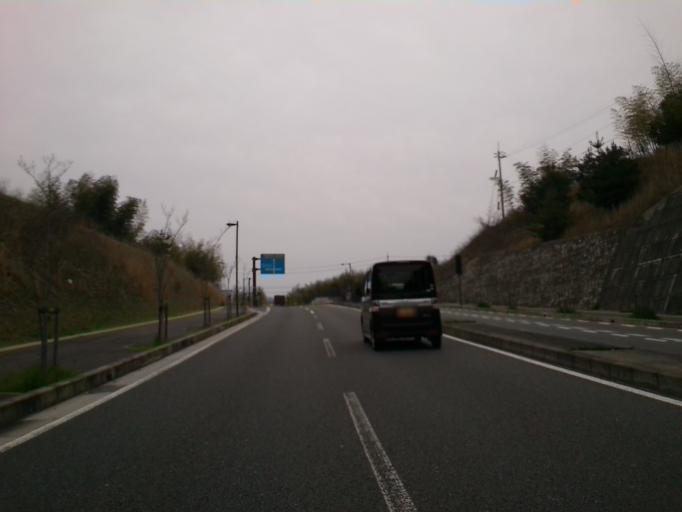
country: JP
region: Kyoto
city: Tanabe
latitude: 34.8196
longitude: 135.7608
